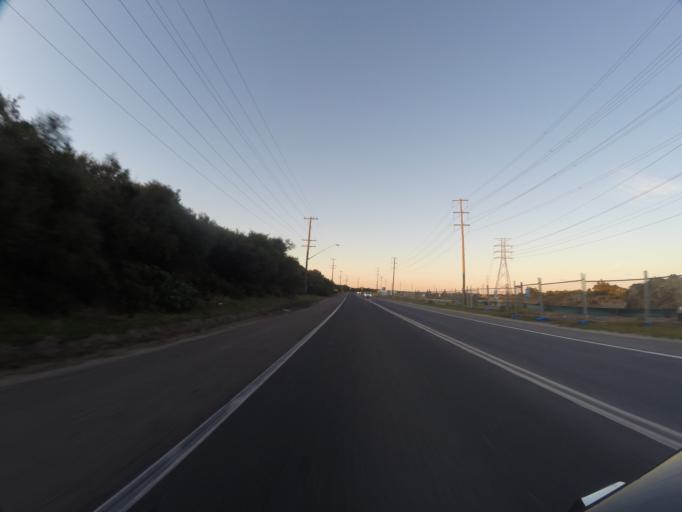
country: AU
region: New South Wales
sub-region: Sutherland Shire
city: Kurnell
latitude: -34.0259
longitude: 151.1812
